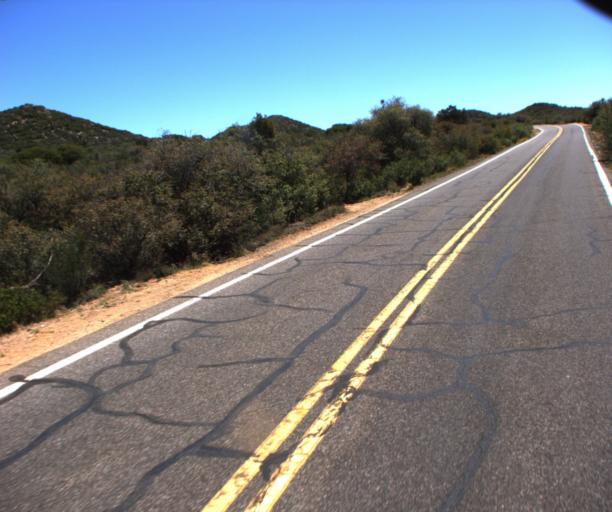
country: US
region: Arizona
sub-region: Yavapai County
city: Prescott
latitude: 34.4241
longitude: -112.5630
